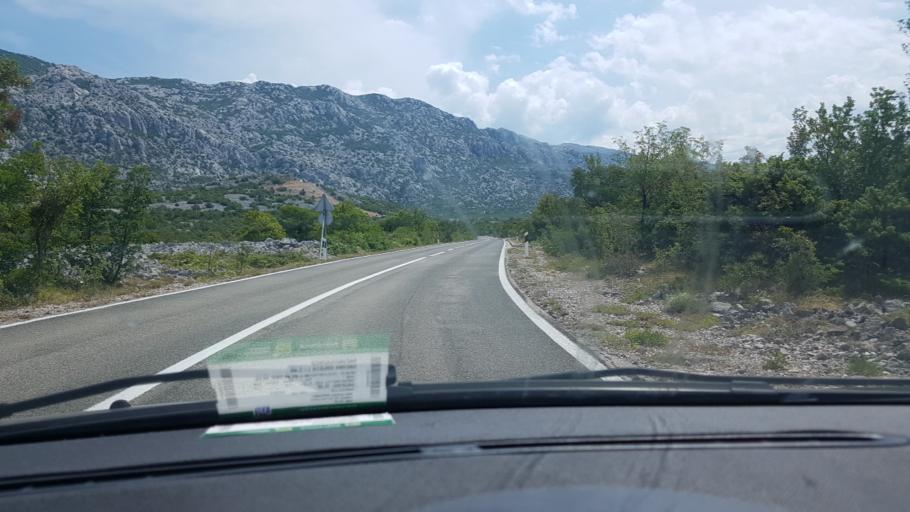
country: HR
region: Primorsko-Goranska
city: Banjol
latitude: 44.7148
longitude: 14.9092
